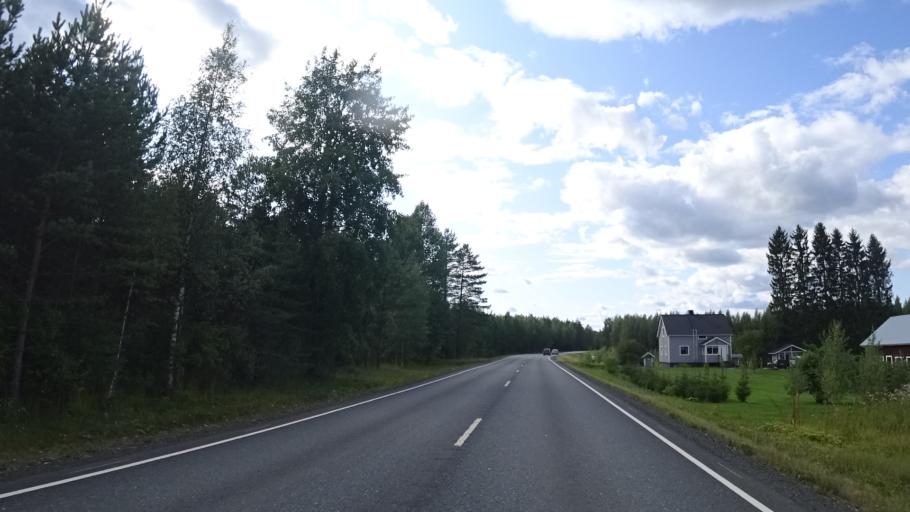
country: FI
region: North Karelia
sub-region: Keski-Karjala
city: Tohmajaervi
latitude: 62.1848
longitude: 30.4750
